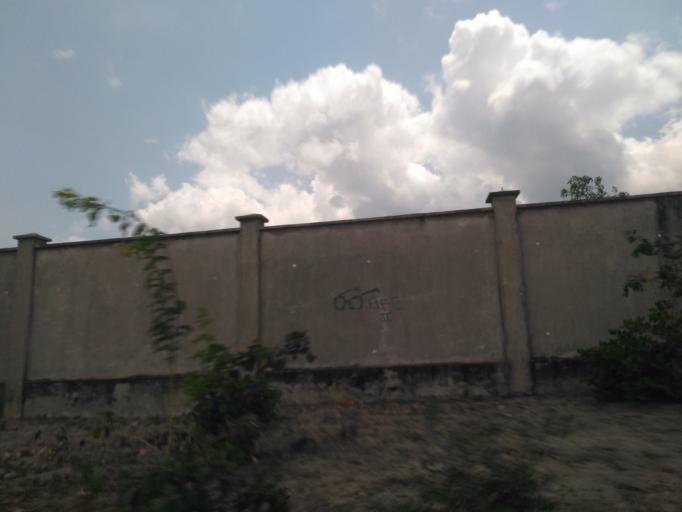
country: TZ
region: Dar es Salaam
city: Dar es Salaam
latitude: -6.8562
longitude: 39.3624
